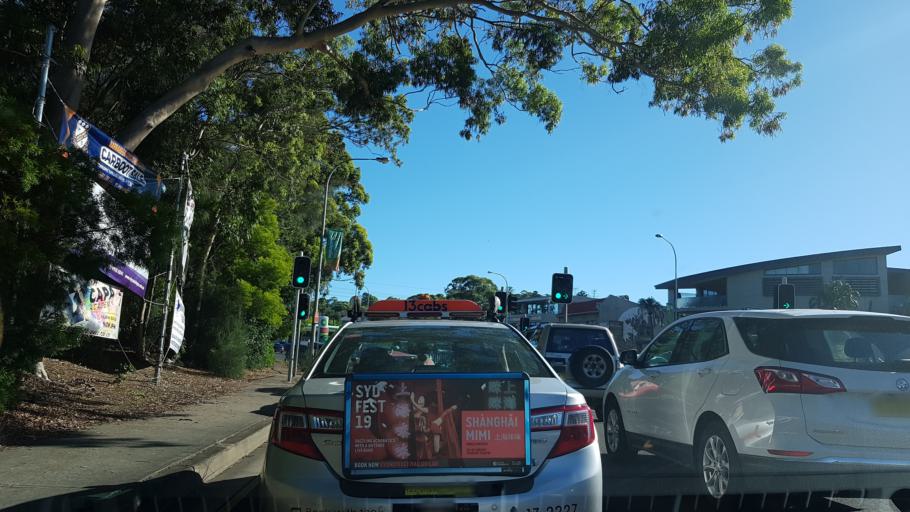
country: AU
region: New South Wales
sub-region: Pittwater
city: Warriewood
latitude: -33.6779
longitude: 151.3040
